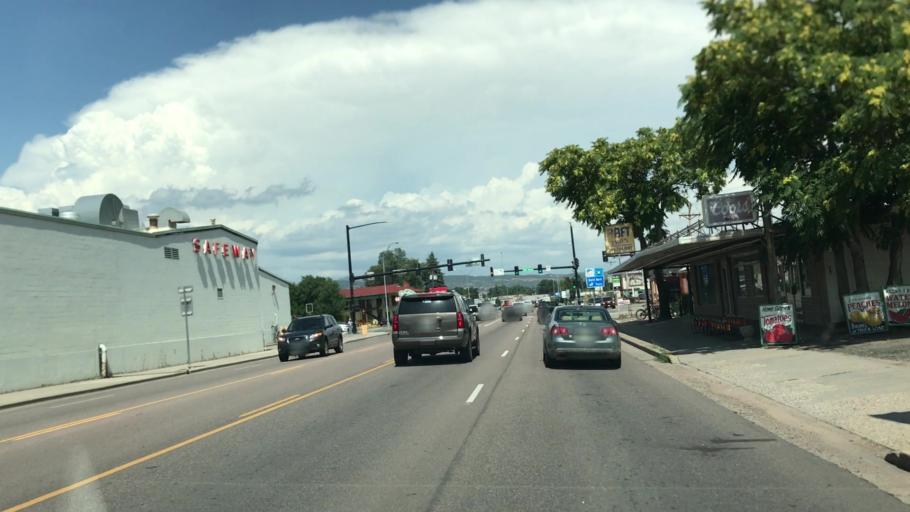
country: US
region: Colorado
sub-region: Fremont County
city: Canon City
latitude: 38.4453
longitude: -105.2282
